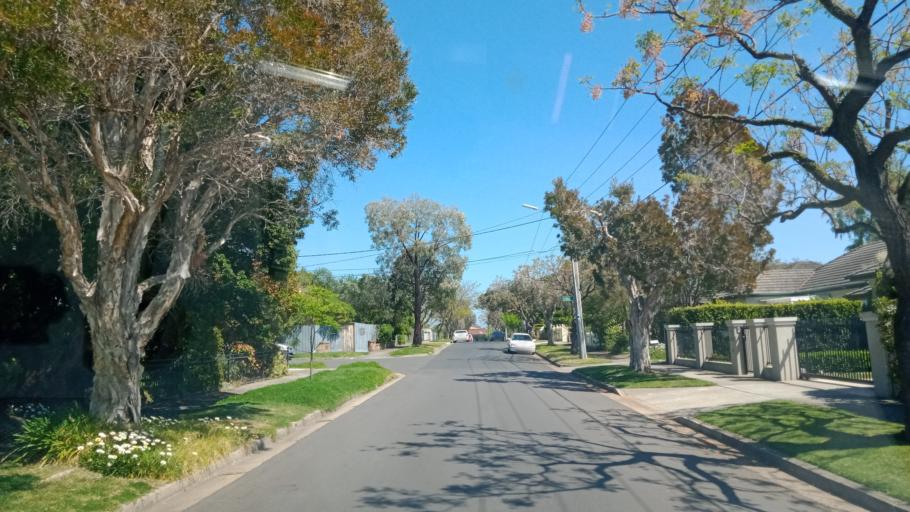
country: AU
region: Victoria
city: Hughesdale
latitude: -37.9154
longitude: 145.0773
